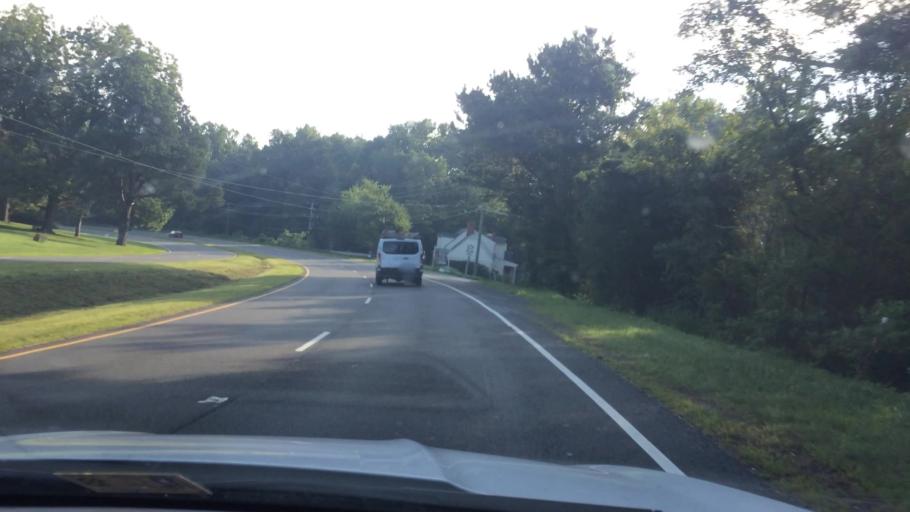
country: US
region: Virginia
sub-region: Gloucester County
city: Gloucester Courthouse
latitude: 37.3992
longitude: -76.5206
